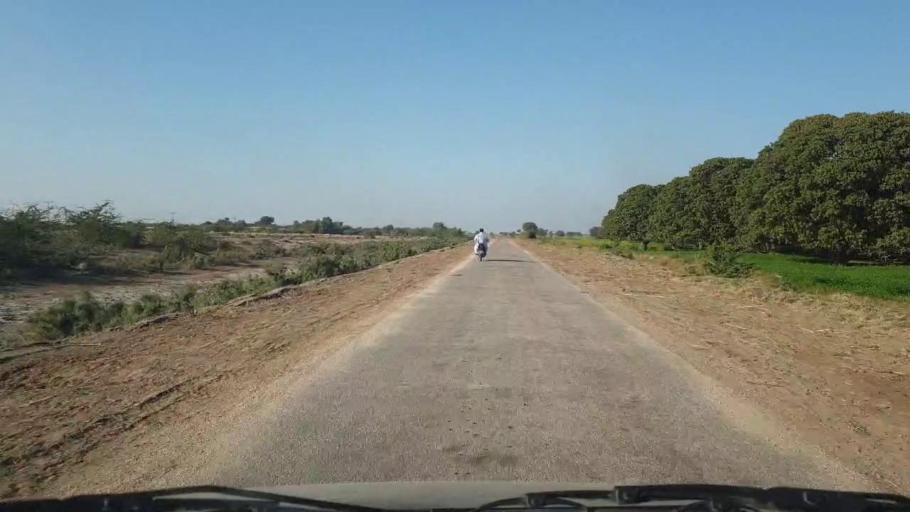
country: PK
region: Sindh
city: Samaro
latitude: 25.3418
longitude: 69.2999
